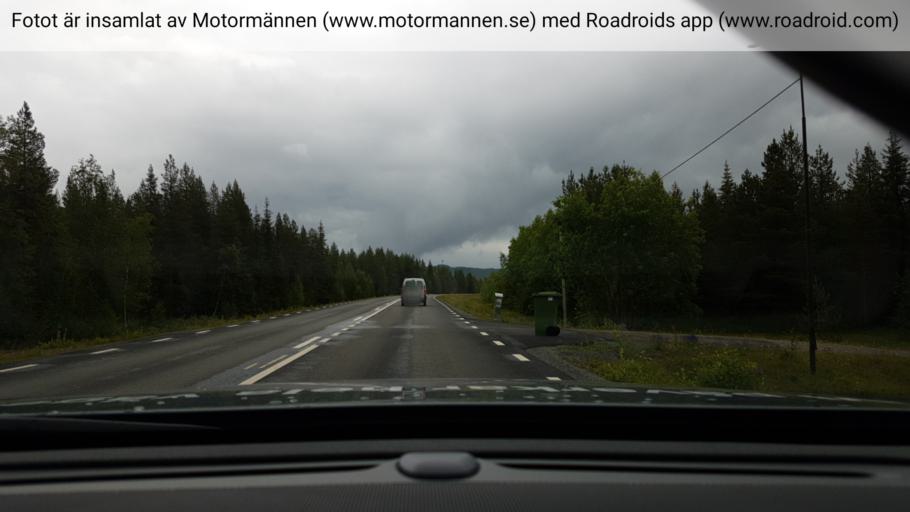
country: SE
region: Vaesterbotten
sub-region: Norsjo Kommun
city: Norsjoe
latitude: 65.2885
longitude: 19.5847
